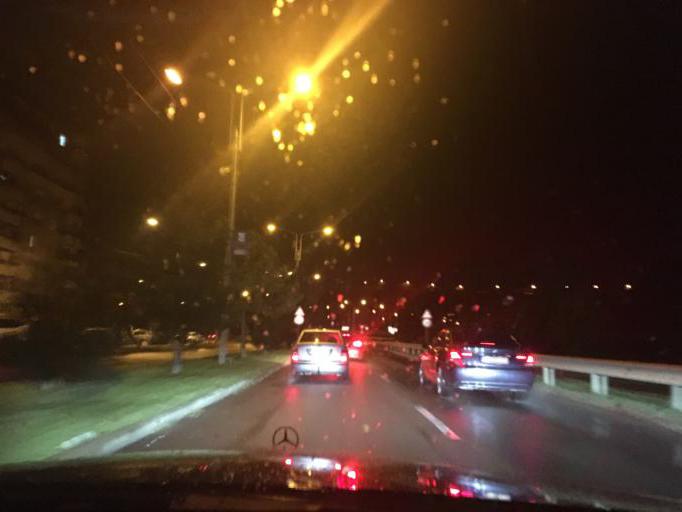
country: RO
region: Bihor
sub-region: Comuna Biharea
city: Oradea
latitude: 47.0495
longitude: 21.9615
